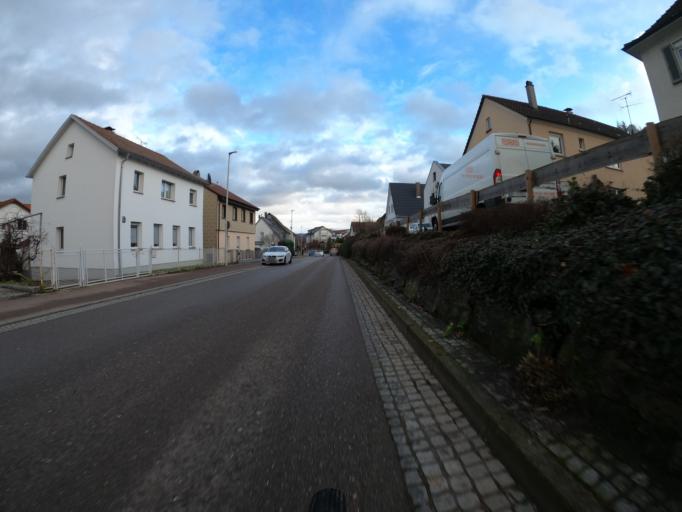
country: DE
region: Baden-Wuerttemberg
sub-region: Regierungsbezirk Stuttgart
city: Eislingen
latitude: 48.6917
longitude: 9.7072
